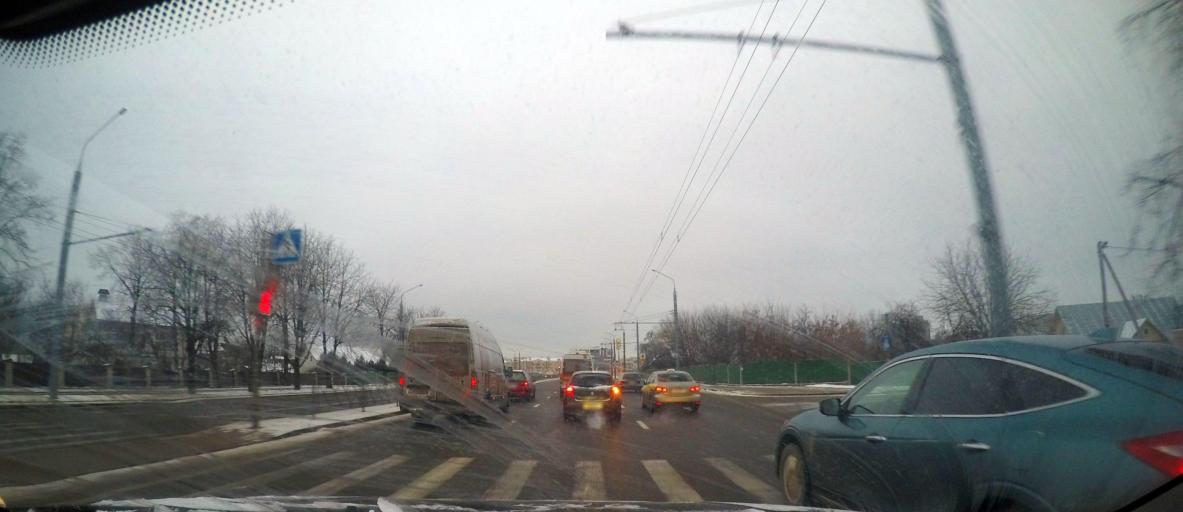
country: BY
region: Grodnenskaya
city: Hrodna
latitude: 53.6671
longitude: 23.8249
